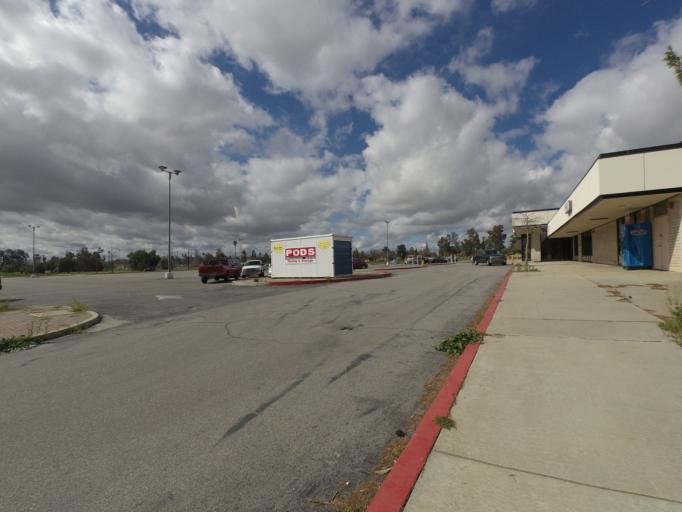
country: US
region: California
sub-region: Riverside County
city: March Air Force Base
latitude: 33.9003
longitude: -117.2491
